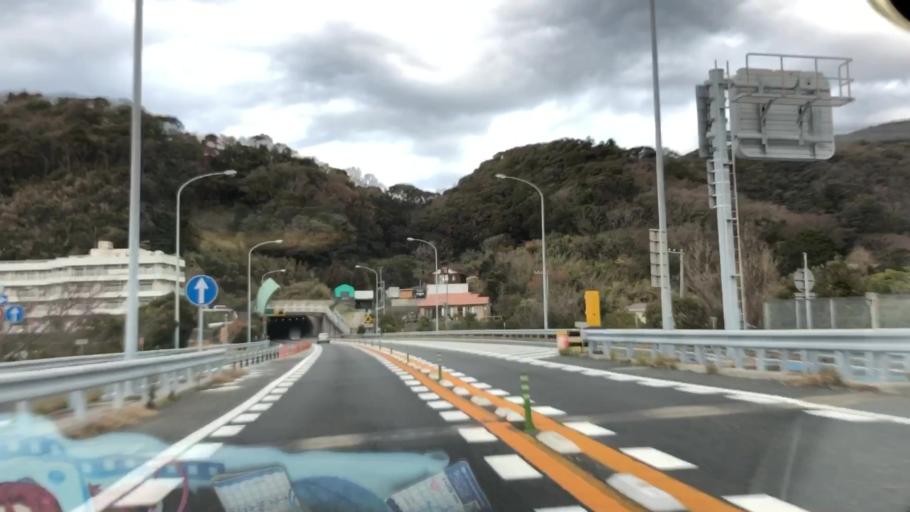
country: JP
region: Chiba
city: Tateyama
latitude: 35.1437
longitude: 139.8477
